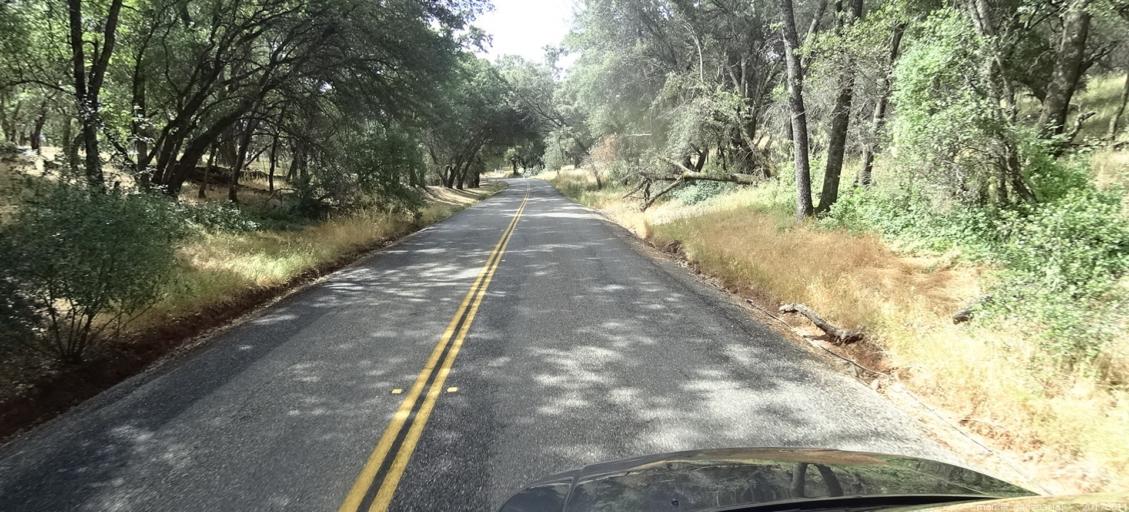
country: US
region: California
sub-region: Yuba County
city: Loma Rica
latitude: 39.3747
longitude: -121.3758
